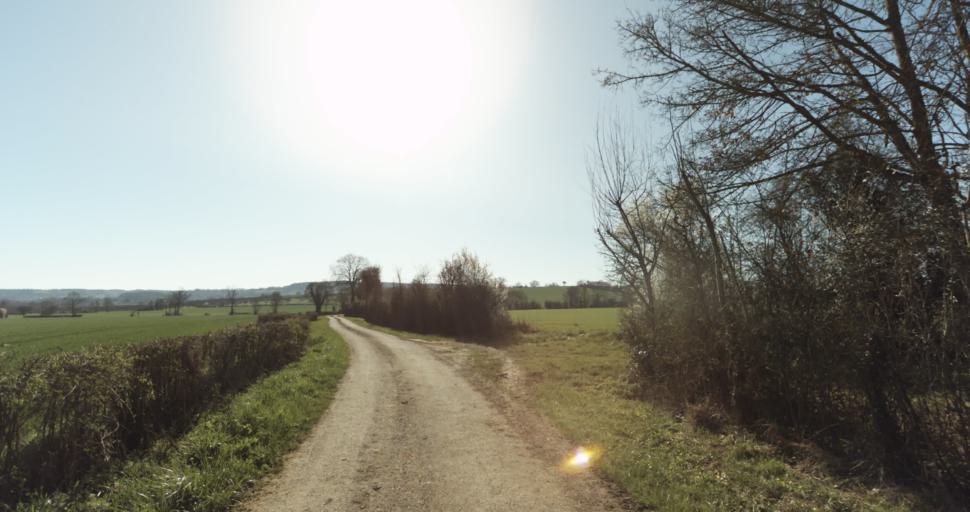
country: FR
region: Lower Normandy
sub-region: Departement du Calvados
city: Saint-Pierre-sur-Dives
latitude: 48.9536
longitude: 0.0188
